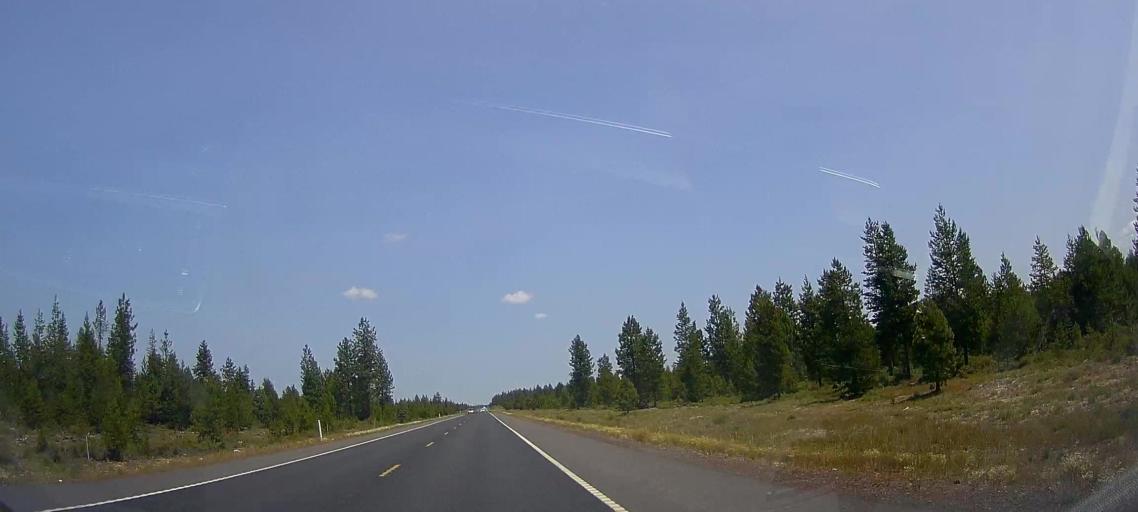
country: US
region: Oregon
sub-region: Deschutes County
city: La Pine
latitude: 43.5022
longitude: -121.6669
